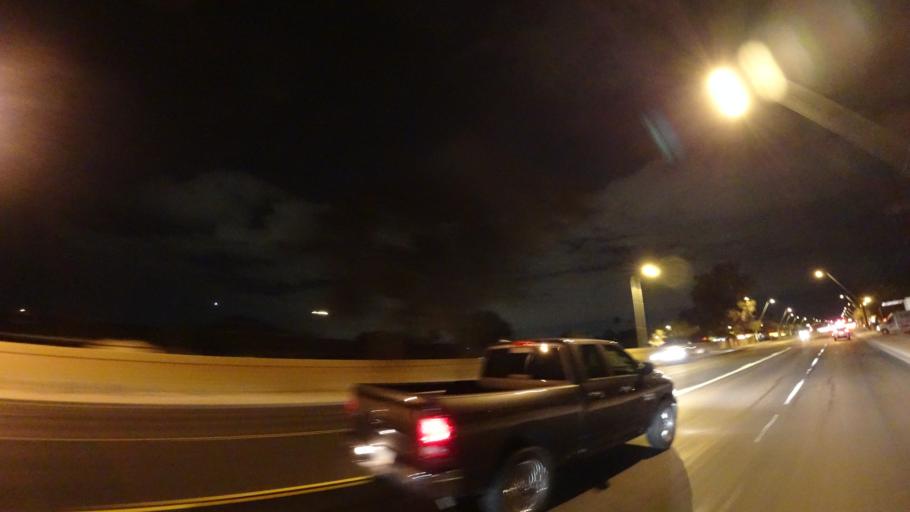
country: US
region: Arizona
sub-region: Maricopa County
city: San Carlos
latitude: 33.3460
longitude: -111.8590
